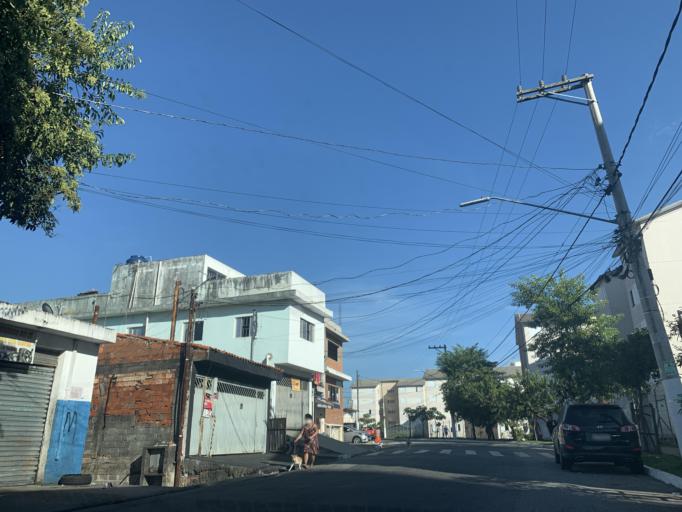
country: BR
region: Sao Paulo
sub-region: Diadema
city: Diadema
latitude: -23.7093
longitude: -46.6529
